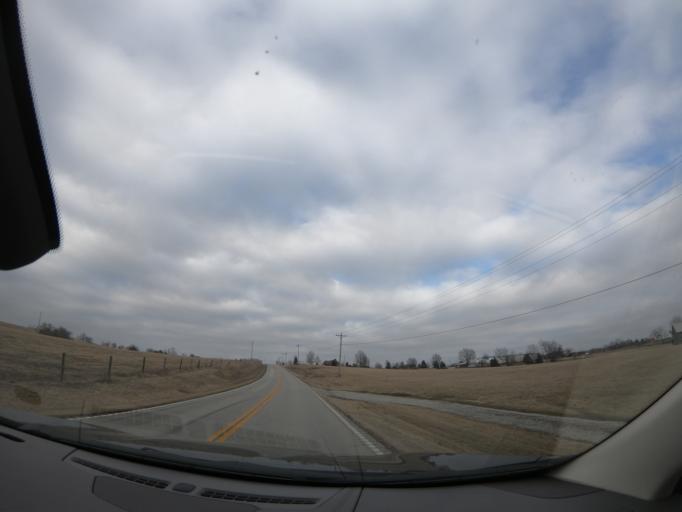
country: US
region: Kentucky
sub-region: Nelson County
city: Bardstown
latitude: 37.8549
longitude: -85.3421
